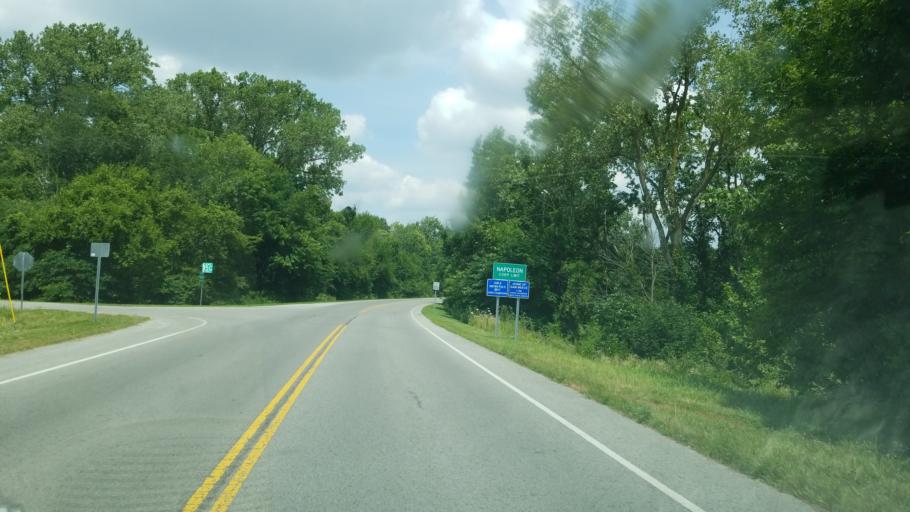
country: US
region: Ohio
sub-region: Henry County
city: Napoleon
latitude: 41.3623
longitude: -84.1533
